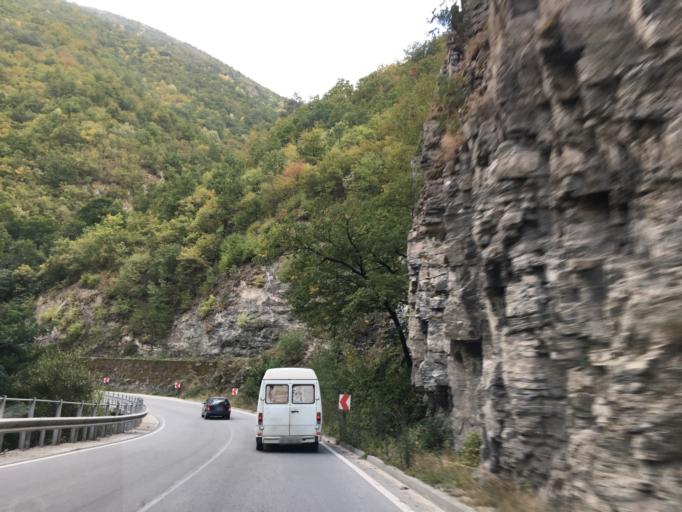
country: BG
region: Pazardzhik
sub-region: Obshtina Septemvri
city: Septemvri
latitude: 42.1024
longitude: 24.0985
